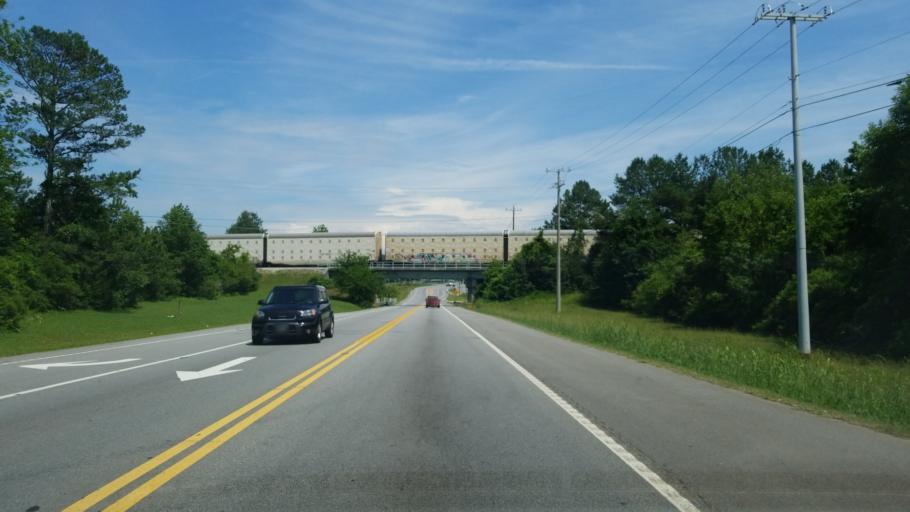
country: US
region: Tennessee
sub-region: Hamilton County
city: Harrison
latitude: 35.0714
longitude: -85.1545
